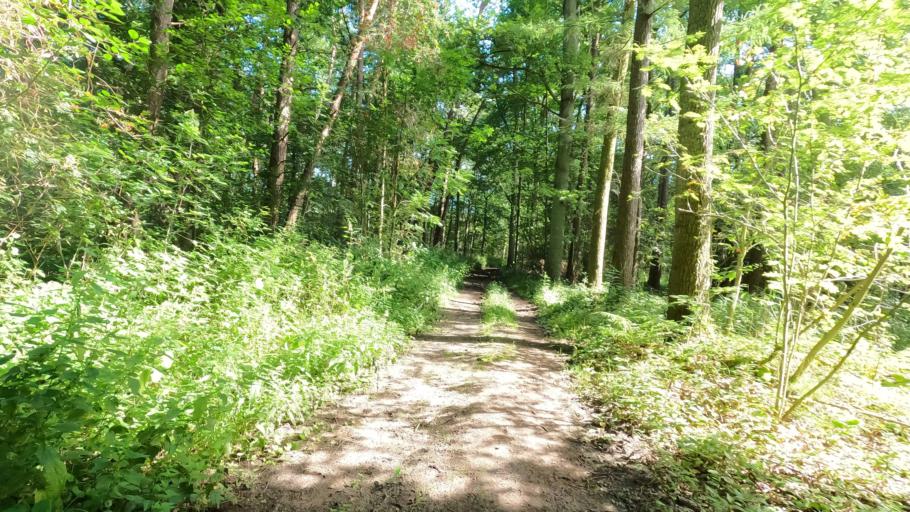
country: BE
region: Flanders
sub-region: Provincie Antwerpen
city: Zandhoven
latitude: 51.2209
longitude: 4.6404
